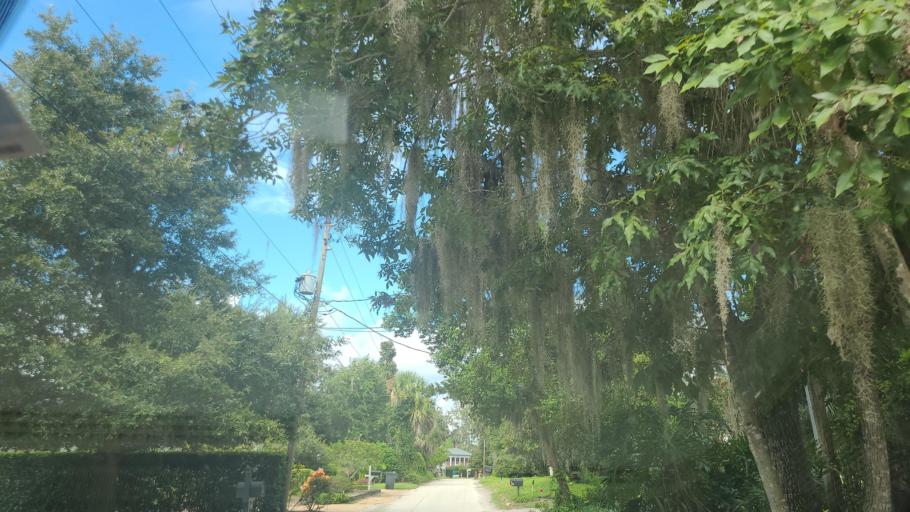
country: US
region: Florida
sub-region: Orange County
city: Lake Butler
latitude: 28.4974
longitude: -81.5430
